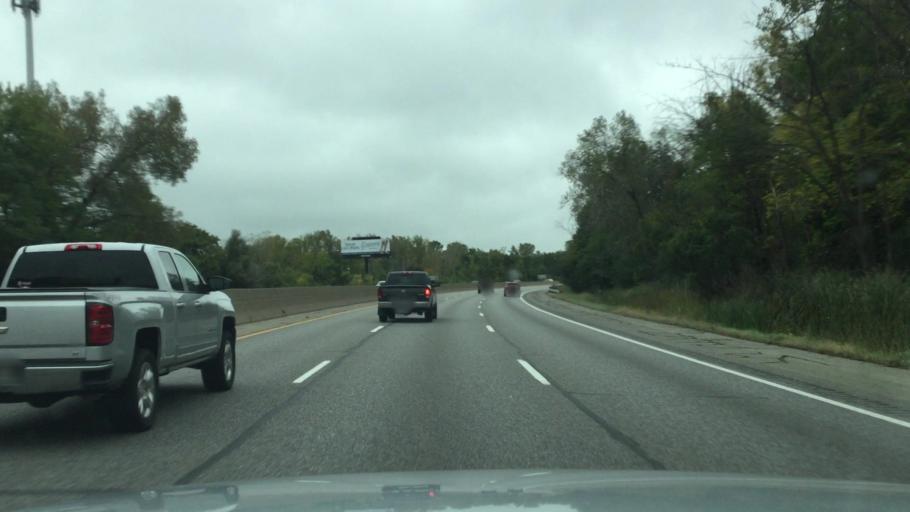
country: US
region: Michigan
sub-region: Genesee County
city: Flint
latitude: 43.0163
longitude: -83.7482
